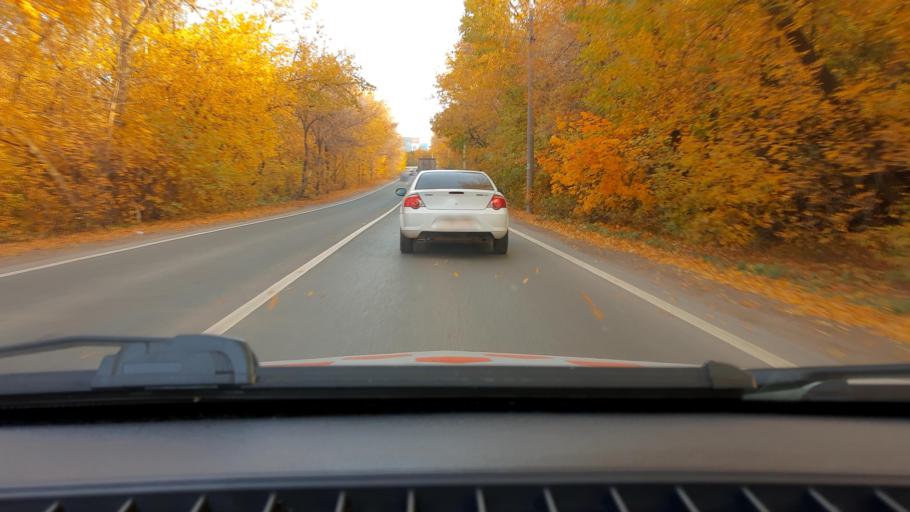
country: RU
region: Bashkortostan
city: Ufa
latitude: 54.8566
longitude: 56.0742
